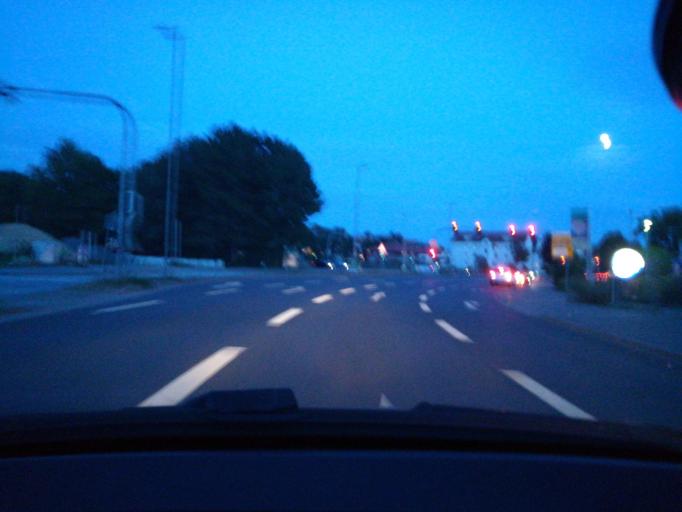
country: DE
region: North Rhine-Westphalia
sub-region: Regierungsbezirk Detmold
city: Minden
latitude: 52.3002
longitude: 8.9105
